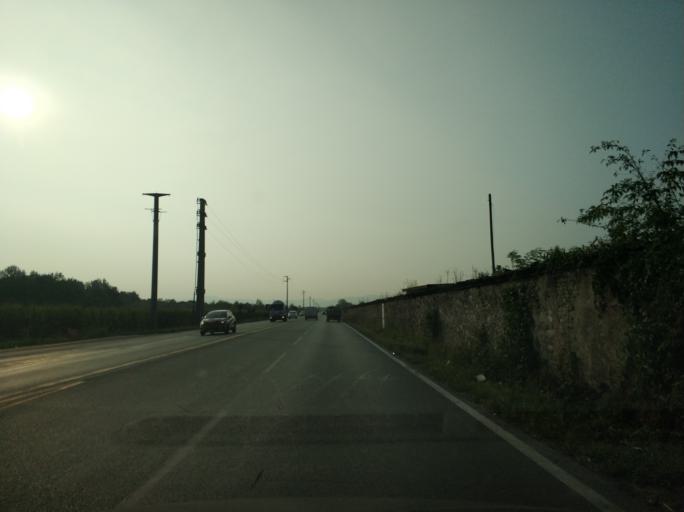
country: IT
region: Piedmont
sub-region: Provincia di Torino
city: Robassomero
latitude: 45.1755
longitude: 7.5843
